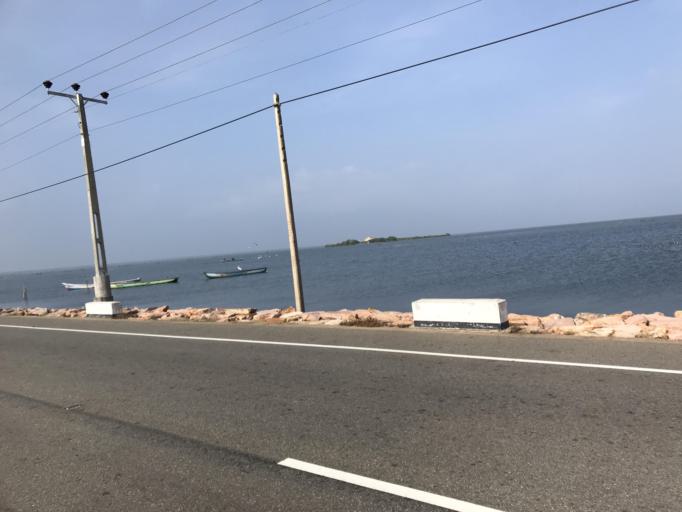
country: LK
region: Northern Province
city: Jaffna
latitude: 9.6536
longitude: 79.9990
